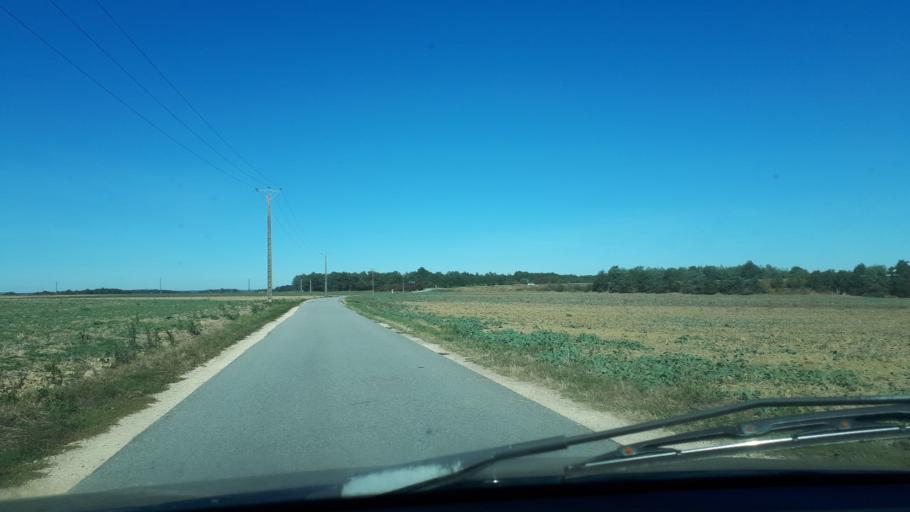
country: FR
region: Centre
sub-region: Departement du Loir-et-Cher
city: Villiers-sur-Loir
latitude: 47.8148
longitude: 1.0140
